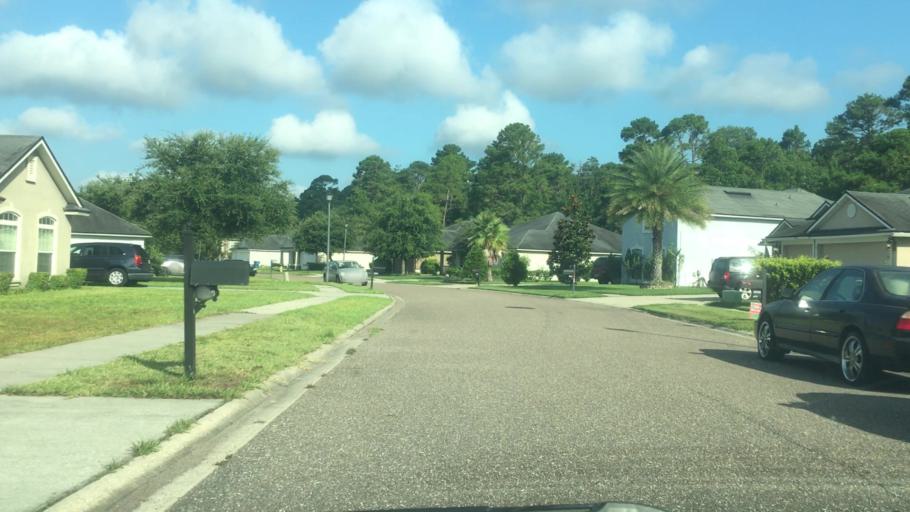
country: US
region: Florida
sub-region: Nassau County
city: Yulee
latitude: 30.4914
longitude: -81.5646
